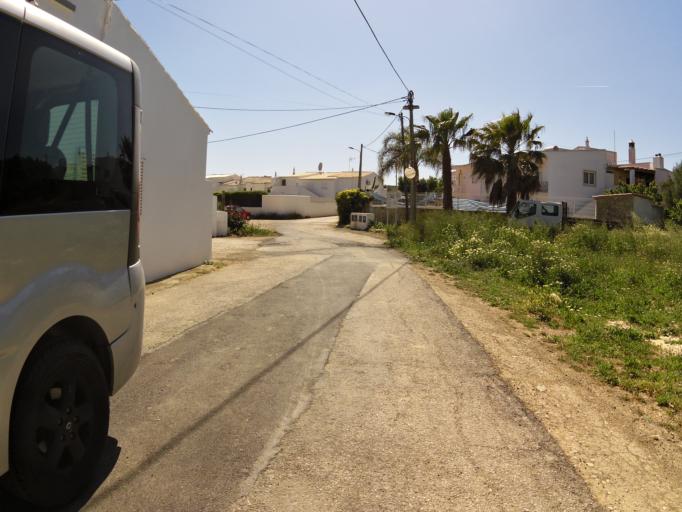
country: PT
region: Faro
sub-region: Lagos
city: Lagos
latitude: 37.1008
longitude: -8.7140
